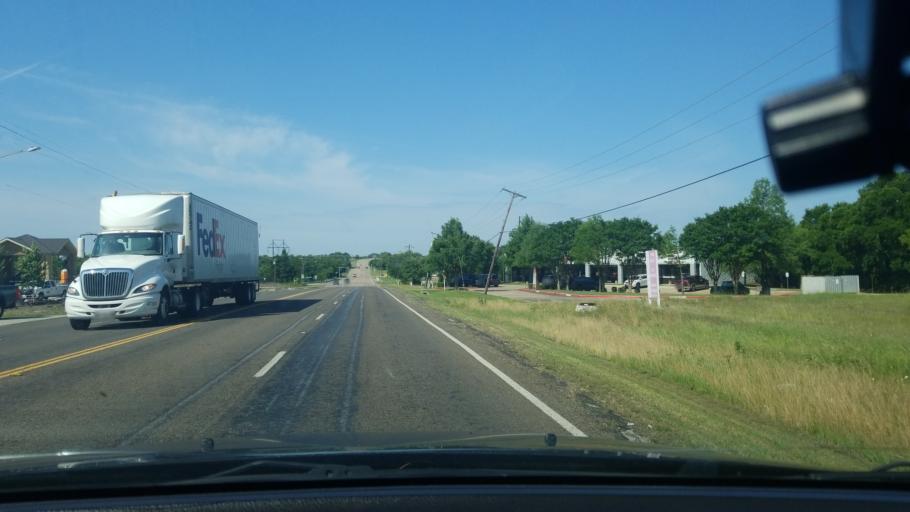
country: US
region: Texas
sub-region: Dallas County
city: Sunnyvale
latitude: 32.7736
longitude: -96.5718
